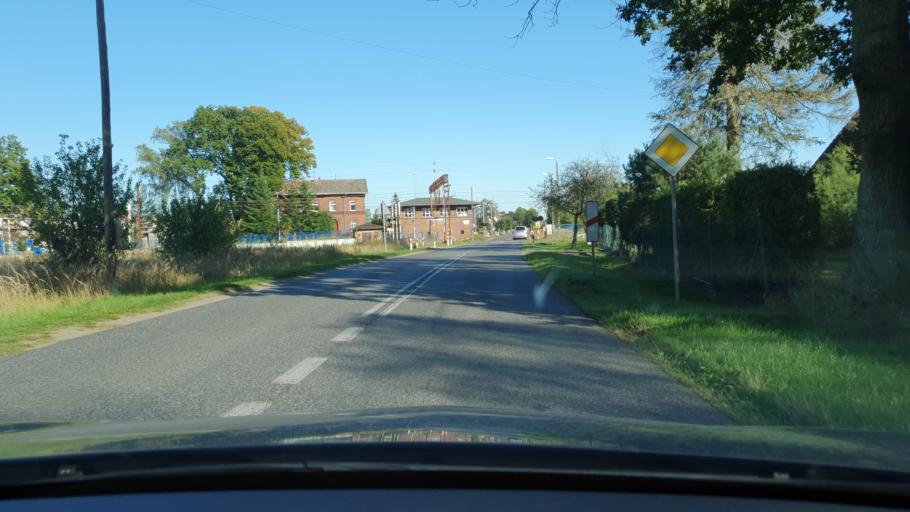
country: PL
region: West Pomeranian Voivodeship
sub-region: Powiat goleniowski
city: Przybiernow
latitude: 53.8245
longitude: 14.8307
